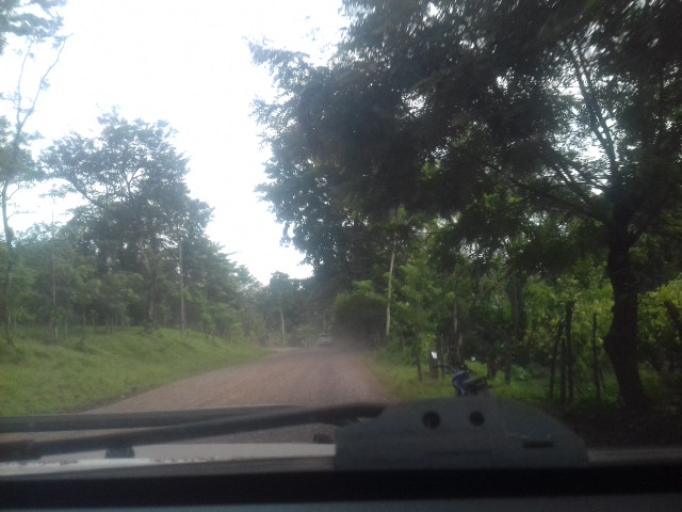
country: NI
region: Atlantico Norte (RAAN)
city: Waslala
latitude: 13.4042
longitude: -85.3204
